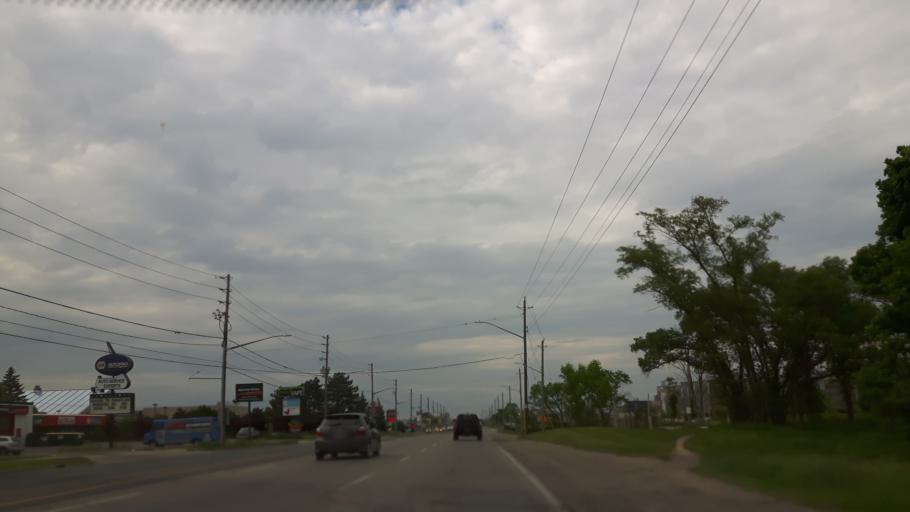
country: CA
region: Ontario
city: London
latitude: 42.9517
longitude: -81.2286
